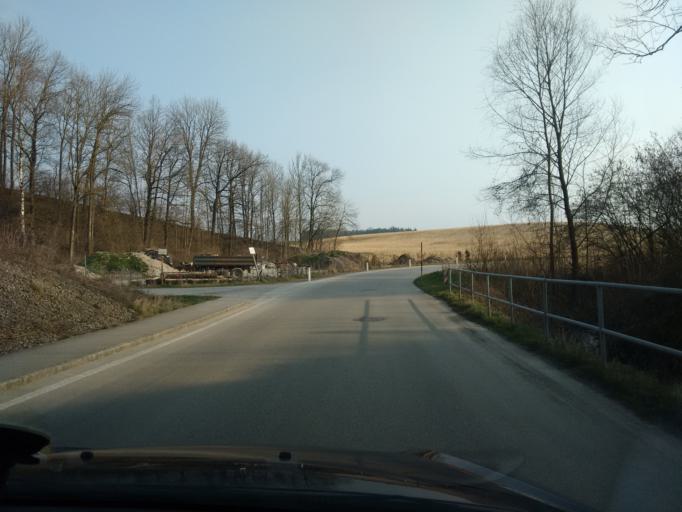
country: AT
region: Upper Austria
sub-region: Politischer Bezirk Grieskirchen
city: Bad Schallerbach
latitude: 48.2150
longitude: 13.9570
